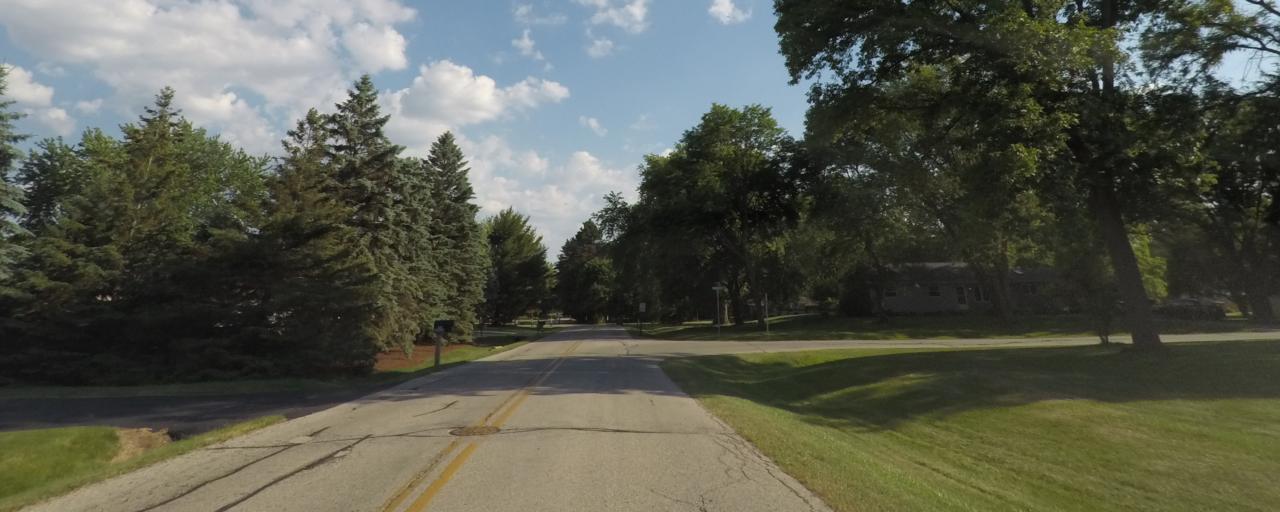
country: US
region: Wisconsin
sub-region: Waukesha County
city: Muskego
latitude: 42.9293
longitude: -88.1035
